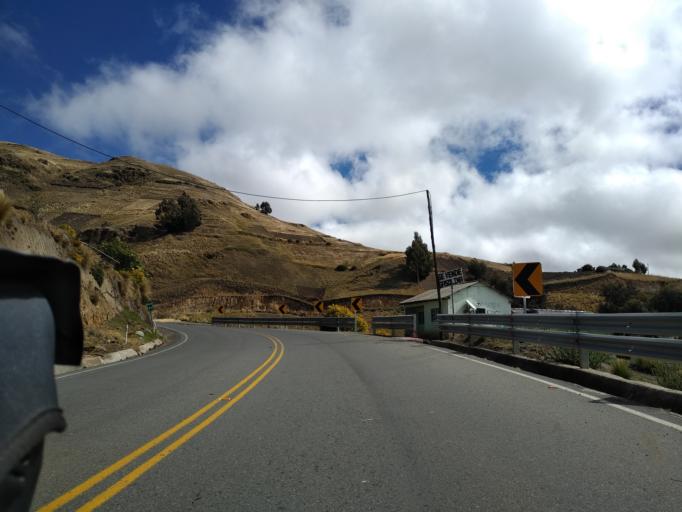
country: EC
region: Cotopaxi
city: Pujili
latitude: -0.9578
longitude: -78.9112
